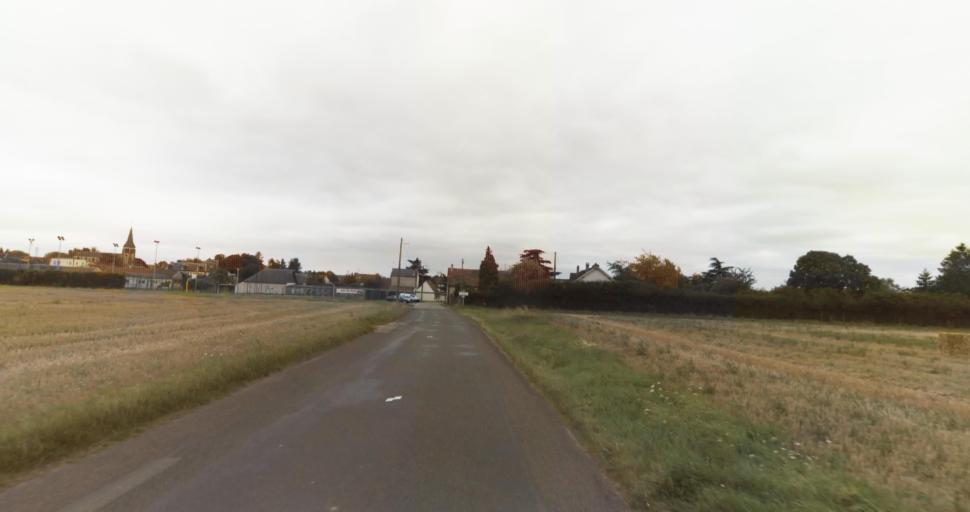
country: FR
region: Haute-Normandie
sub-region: Departement de l'Eure
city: La Couture-Boussey
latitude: 48.9001
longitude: 1.4058
